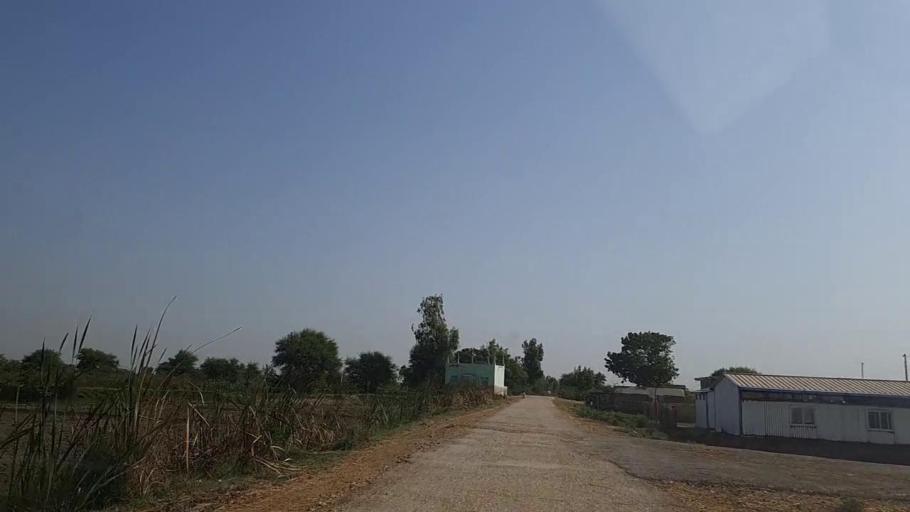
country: PK
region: Sindh
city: Daro Mehar
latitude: 24.7210
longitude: 68.0974
